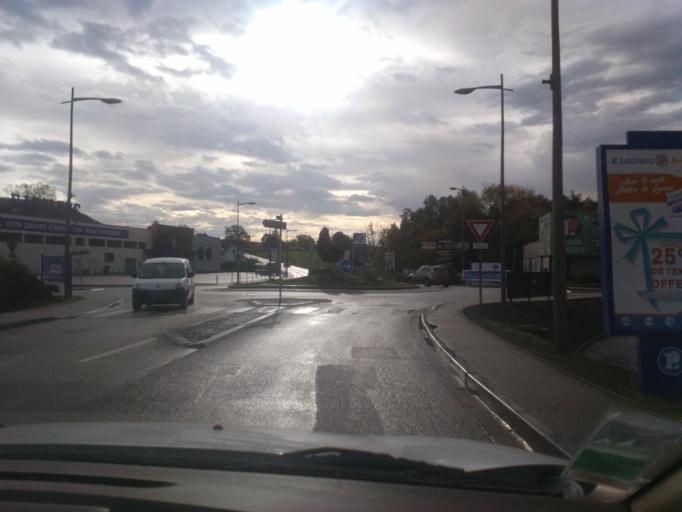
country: FR
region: Lorraine
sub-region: Departement des Vosges
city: Bruyeres
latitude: 48.1995
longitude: 6.7264
